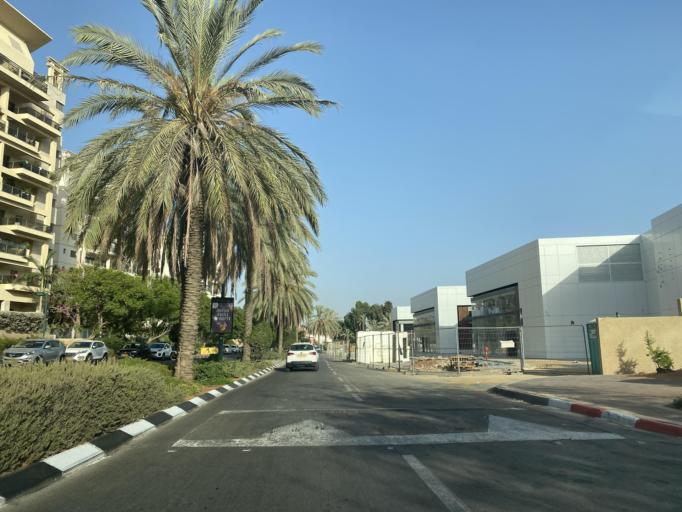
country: IL
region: Central District
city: Kfar Saba
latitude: 32.1635
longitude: 34.9082
